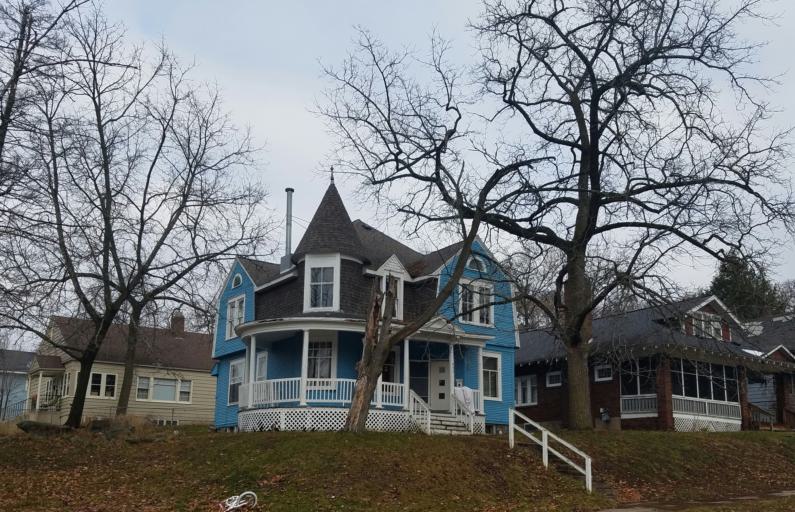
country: US
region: Michigan
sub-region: Wexford County
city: Cadillac
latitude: 44.2489
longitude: -85.3967
